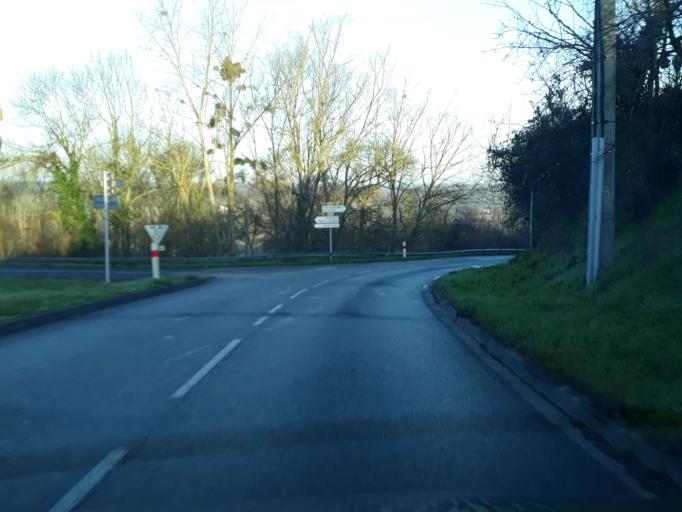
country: FR
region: Midi-Pyrenees
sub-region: Departement de la Haute-Garonne
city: Berat
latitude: 43.3801
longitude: 1.1758
